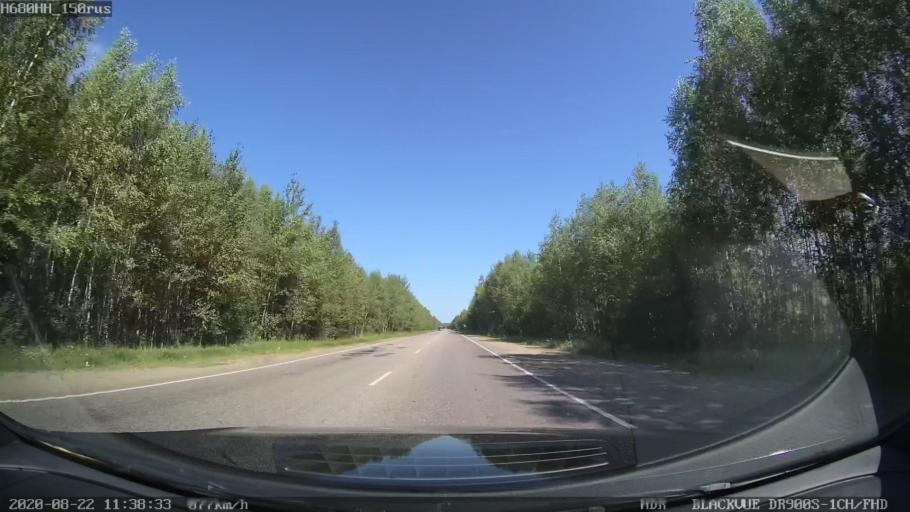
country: RU
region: Tverskaya
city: Sakharovo
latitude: 56.9554
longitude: 36.0164
